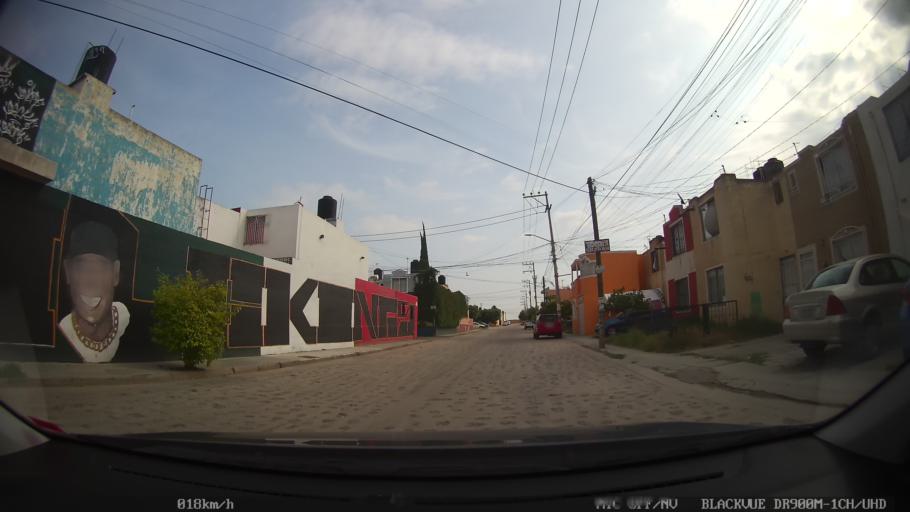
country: MX
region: Jalisco
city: Tonala
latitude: 20.6319
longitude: -103.2346
